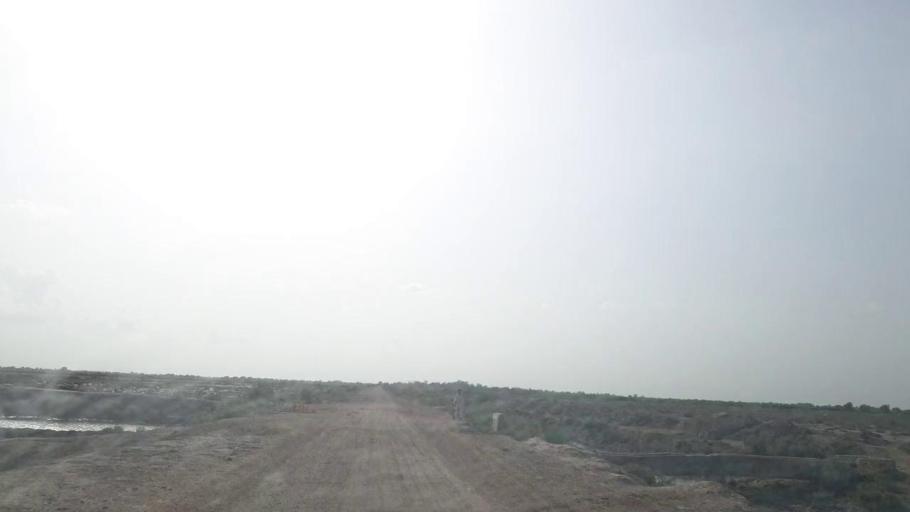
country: PK
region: Sindh
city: Tando Bago
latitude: 24.8164
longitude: 69.1455
